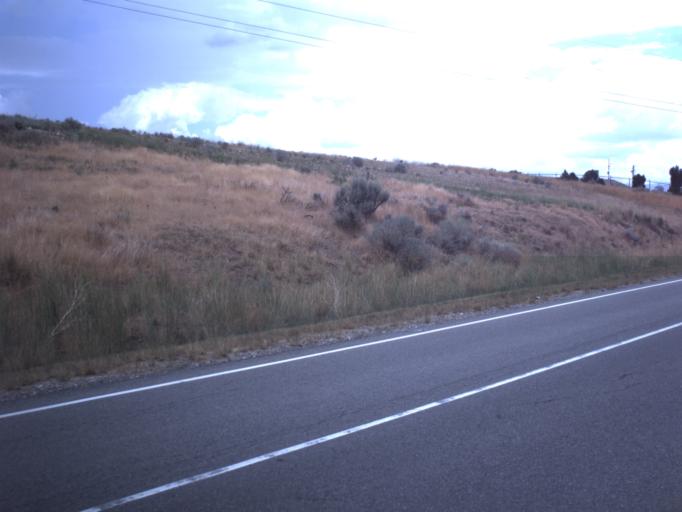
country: US
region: Utah
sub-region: Salt Lake County
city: Herriman
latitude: 40.5664
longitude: -112.0829
